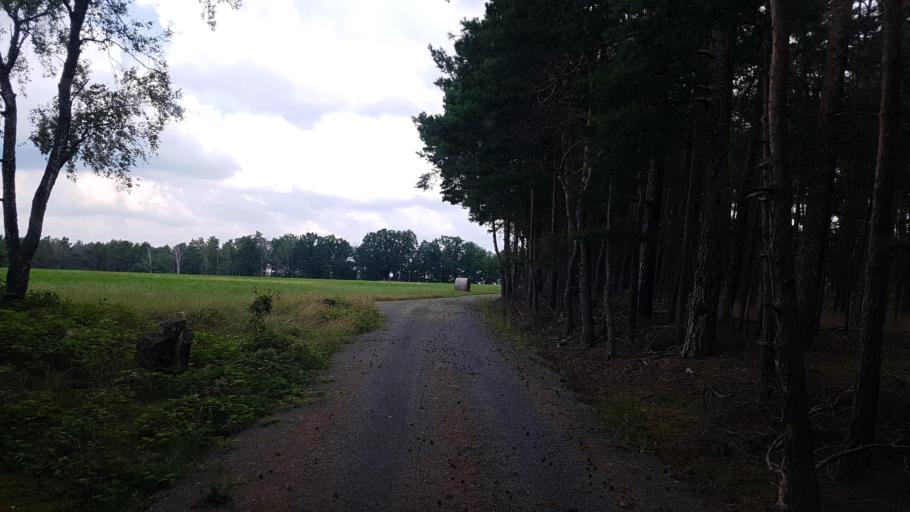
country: DE
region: Brandenburg
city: Crinitz
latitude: 51.7090
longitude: 13.8196
